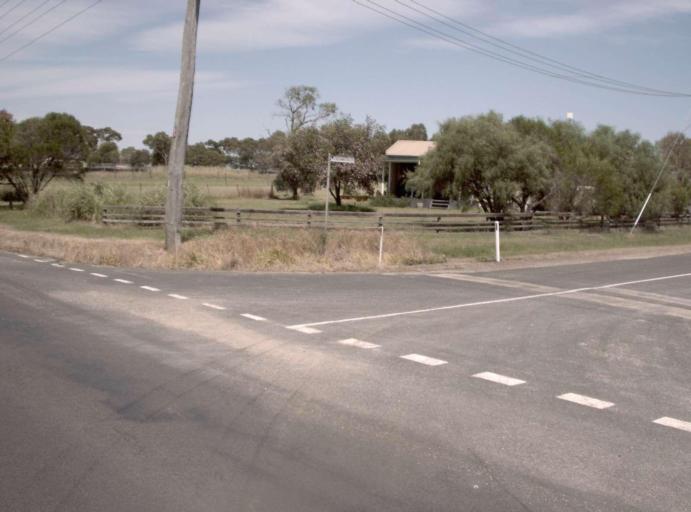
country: AU
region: Victoria
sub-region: Wellington
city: Sale
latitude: -38.1053
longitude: 146.9130
